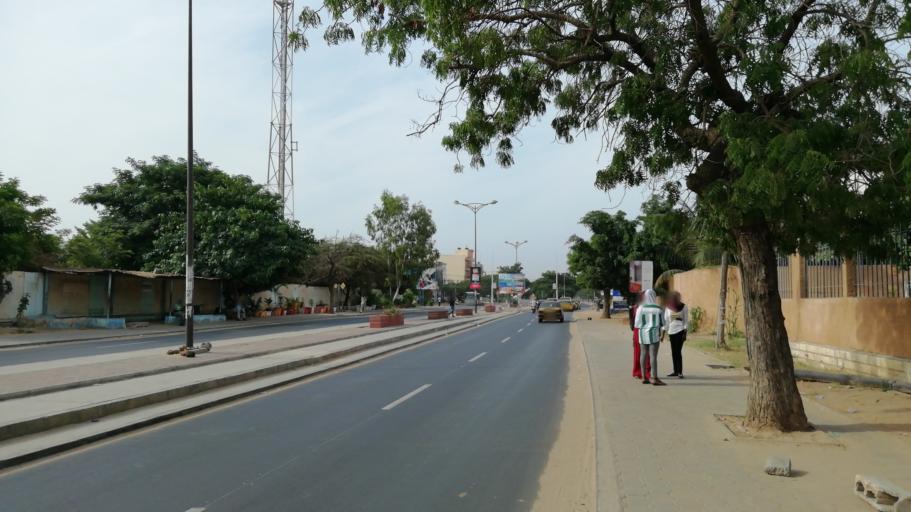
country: SN
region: Dakar
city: Dakar
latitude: 14.6978
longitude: -17.4506
